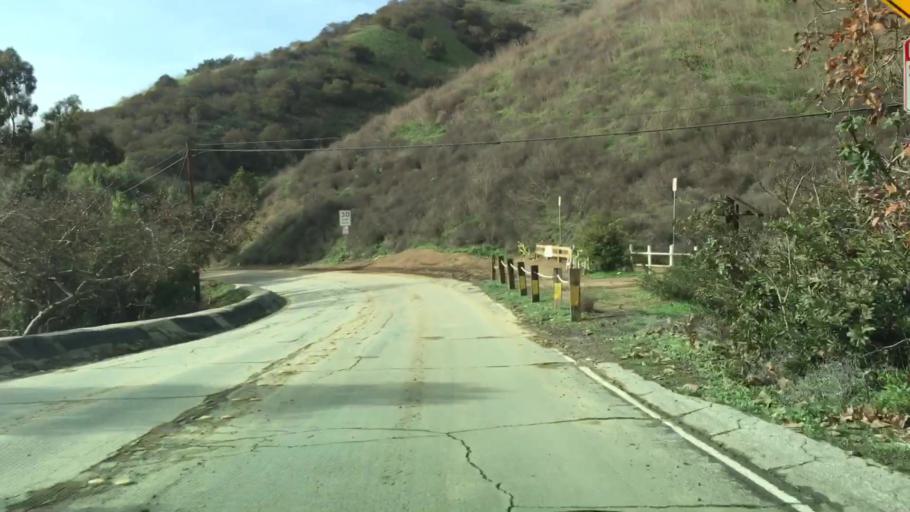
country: US
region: California
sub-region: Los Angeles County
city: Whittier
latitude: 33.9885
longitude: -118.0232
